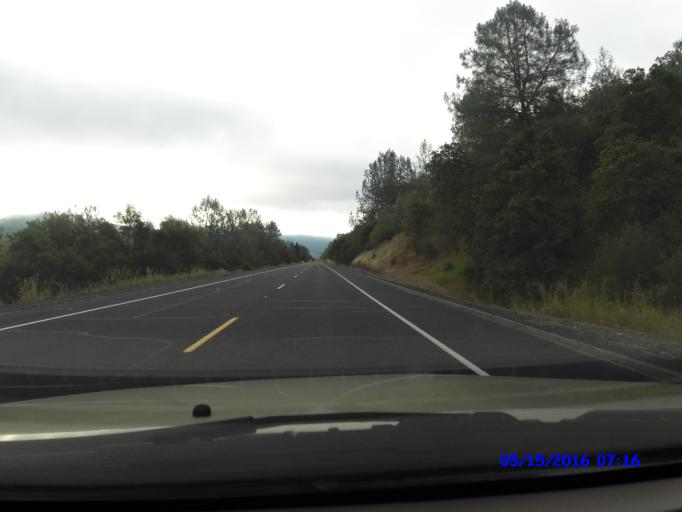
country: US
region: California
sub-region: Tuolumne County
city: East Sonora
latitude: 37.8236
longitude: -120.3330
